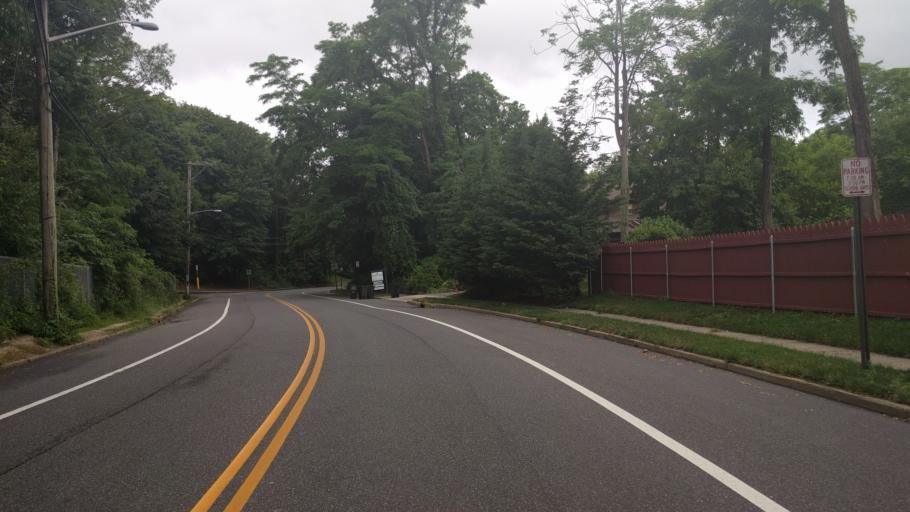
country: US
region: New York
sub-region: Suffolk County
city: Huntington
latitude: 40.8582
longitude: -73.4252
